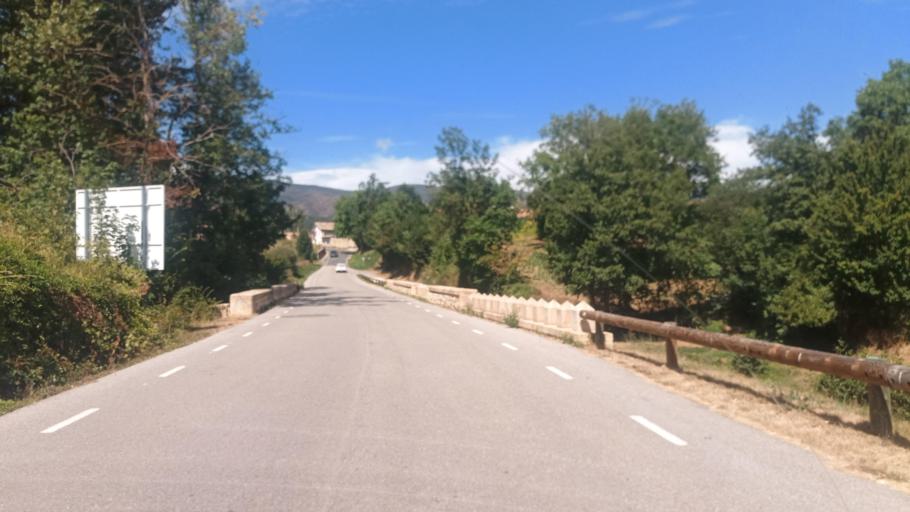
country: ES
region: Castille and Leon
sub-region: Provincia de Burgos
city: Espinosa de los Monteros
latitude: 43.0381
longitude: -3.6658
